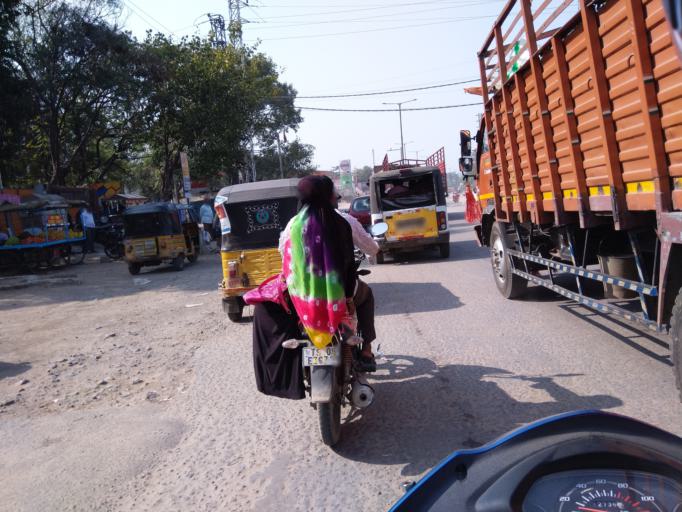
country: IN
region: Telangana
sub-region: Rangareddi
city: Quthbullapur
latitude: 17.5266
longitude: 78.4401
